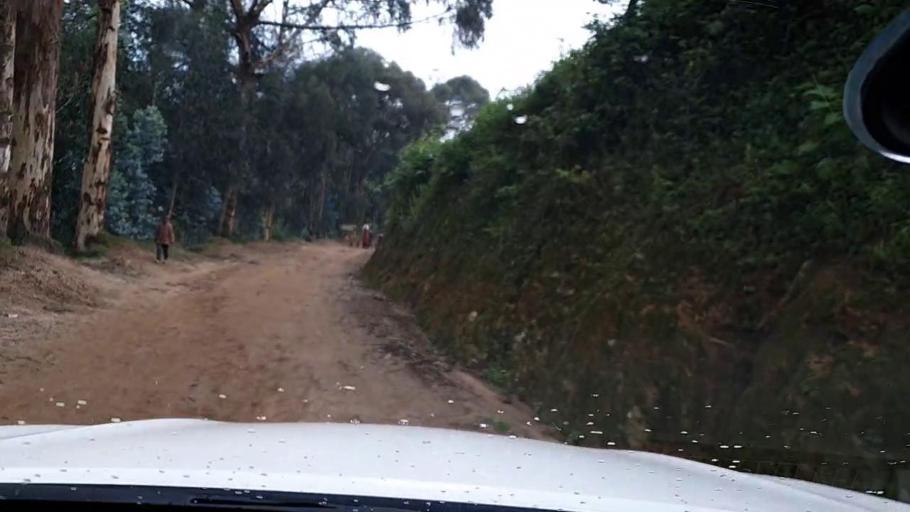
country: RW
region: Southern Province
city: Nzega
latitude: -2.3780
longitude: 29.2457
